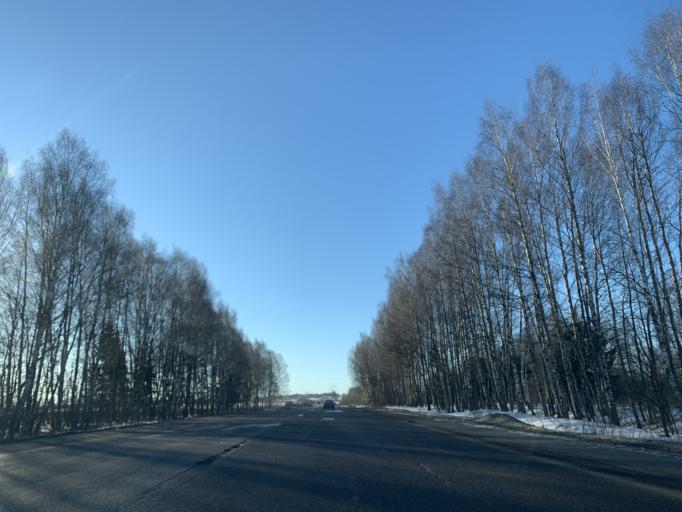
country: RU
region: Jaroslavl
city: Konstantinovskiy
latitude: 57.8024
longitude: 39.5927
